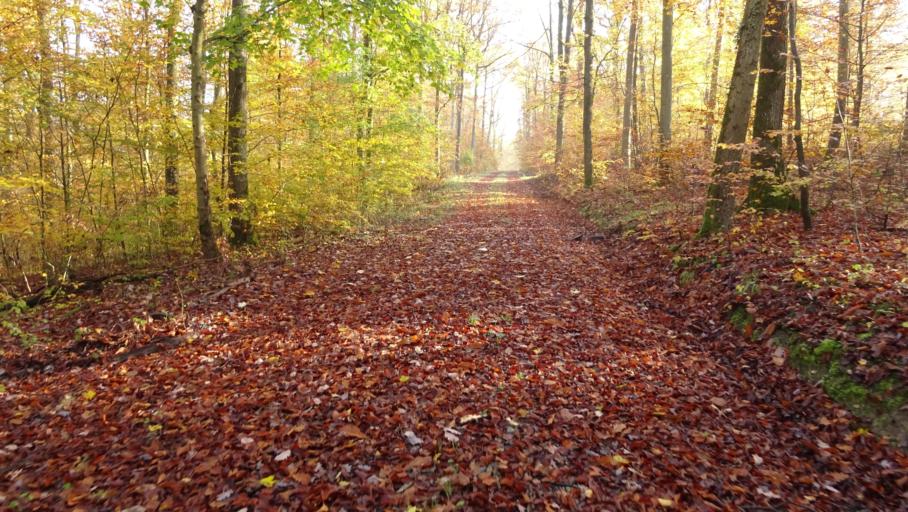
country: DE
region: Baden-Wuerttemberg
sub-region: Karlsruhe Region
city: Obrigheim
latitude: 49.3771
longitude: 9.0941
